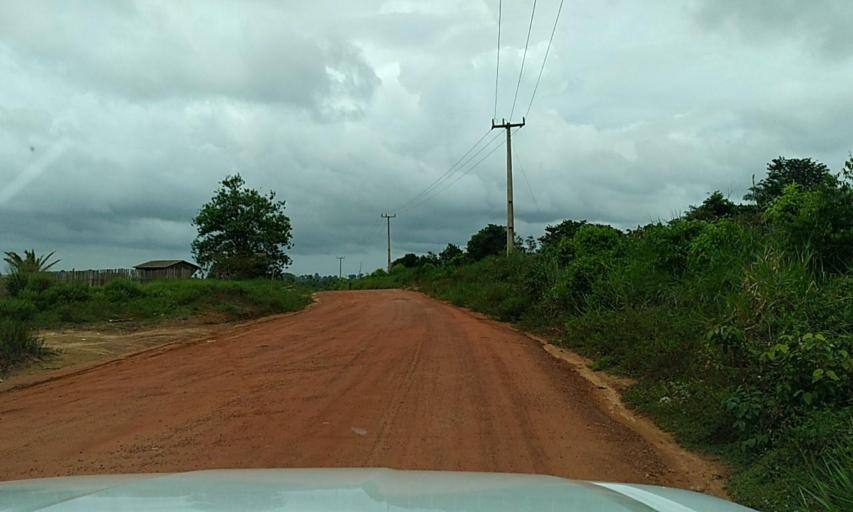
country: BR
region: Para
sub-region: Senador Jose Porfirio
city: Senador Jose Porfirio
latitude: -2.6188
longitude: -51.8667
